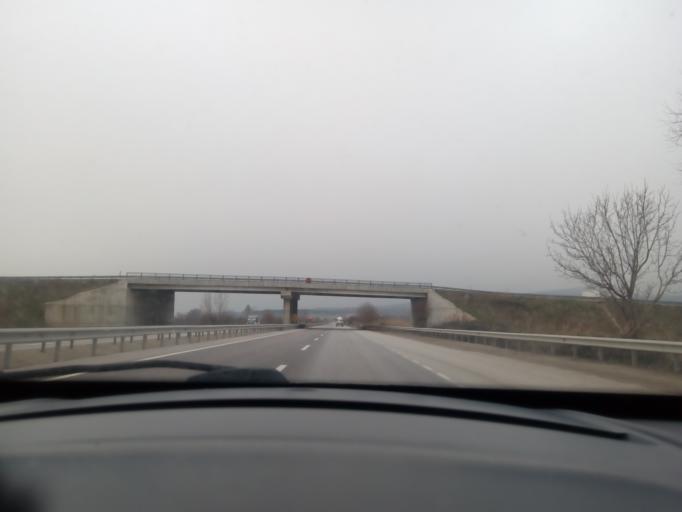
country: TR
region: Balikesir
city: Gobel
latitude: 39.9869
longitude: 28.1977
